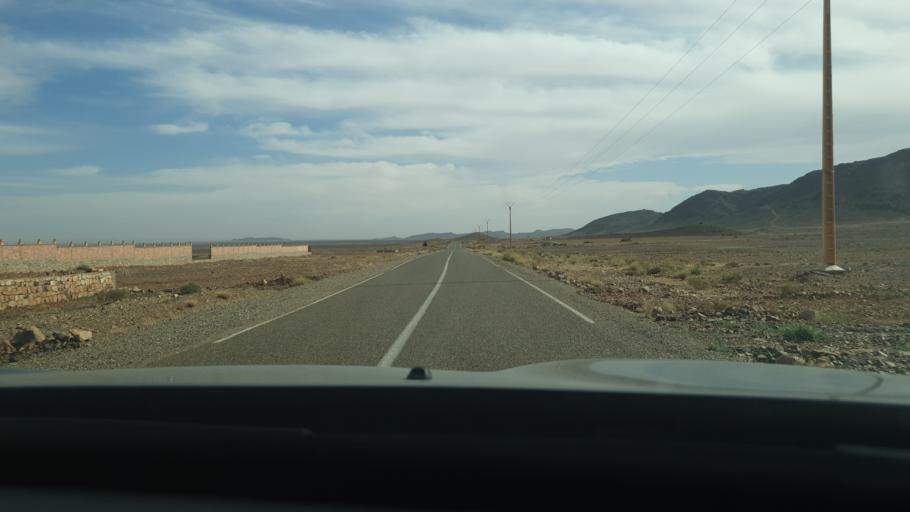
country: MA
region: Meknes-Tafilalet
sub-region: Errachidia
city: Fezna
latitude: 31.5284
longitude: -4.6360
